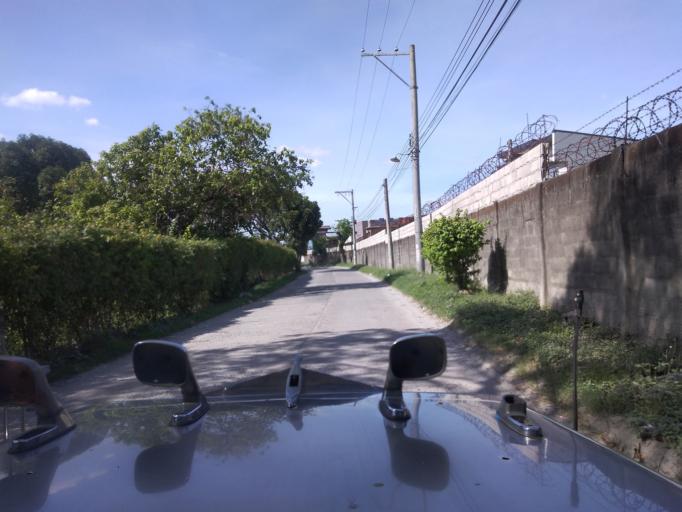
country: PH
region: Central Luzon
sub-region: Province of Pampanga
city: Magliman
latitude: 15.0397
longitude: 120.6601
